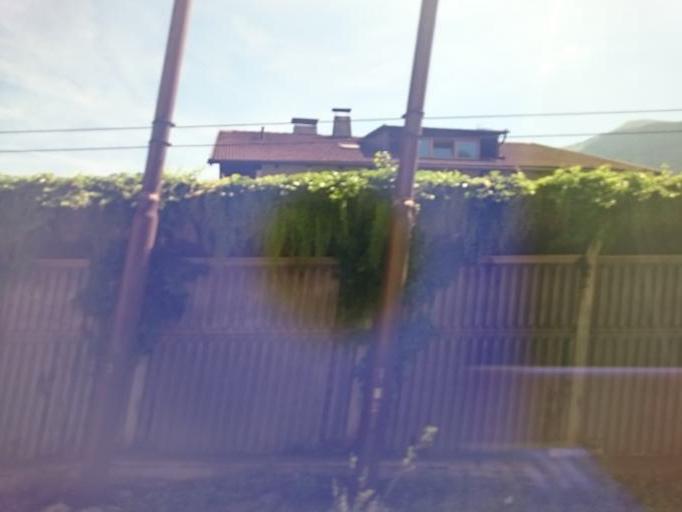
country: IT
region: Trentino-Alto Adige
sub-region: Bolzano
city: Bressanone
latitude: 46.7163
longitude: 11.6496
